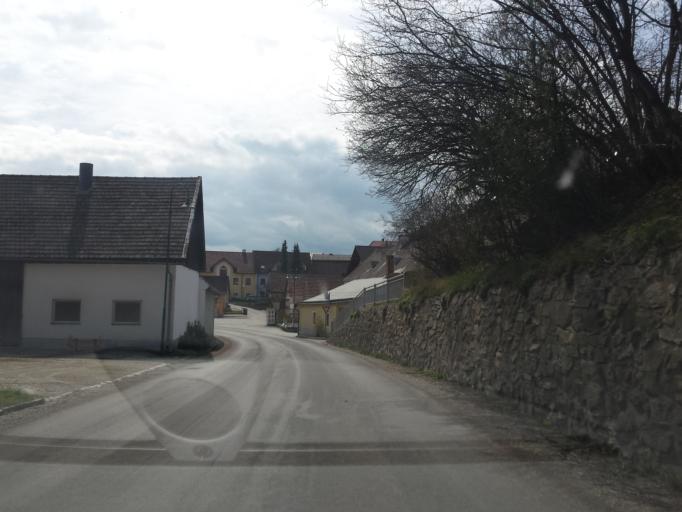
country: AT
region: Lower Austria
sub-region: Politischer Bezirk Krems
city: Rastenfeld
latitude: 48.5454
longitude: 15.3484
